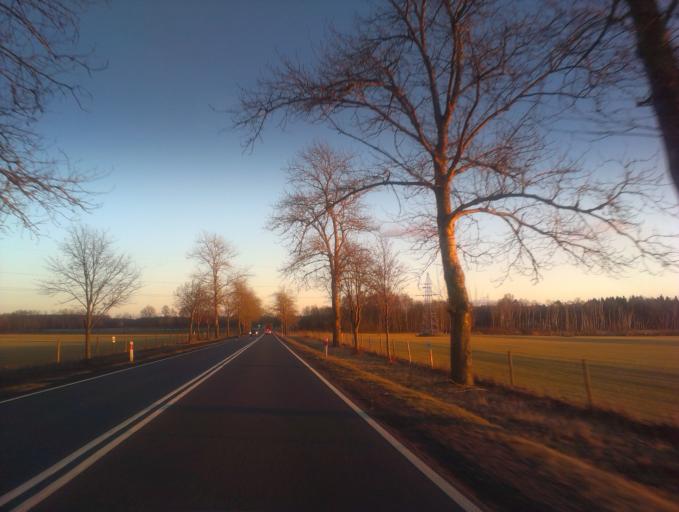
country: PL
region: West Pomeranian Voivodeship
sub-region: Powiat szczecinecki
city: Szczecinek
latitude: 53.6463
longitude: 16.7533
